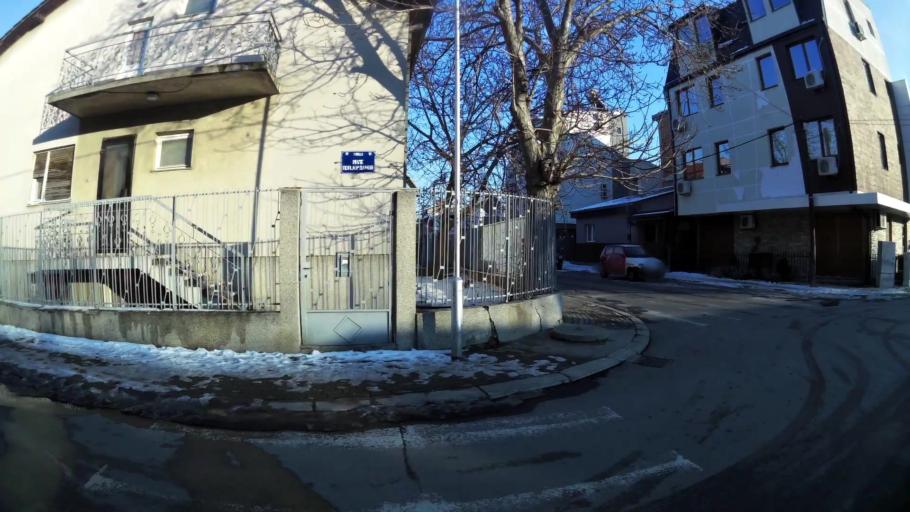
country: MK
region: Karpos
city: Skopje
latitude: 41.9948
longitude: 21.3994
